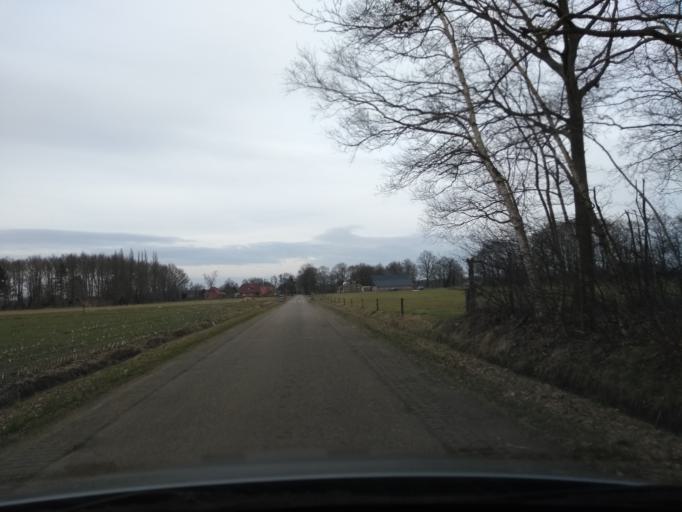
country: NL
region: Overijssel
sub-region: Gemeente Borne
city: Borne
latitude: 52.3480
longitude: 6.7342
